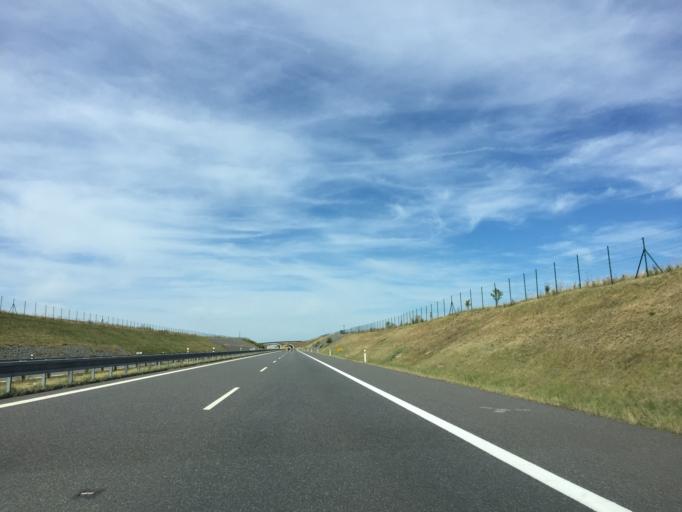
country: CZ
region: Jihocesky
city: Sobeslav
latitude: 49.2997
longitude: 14.7369
